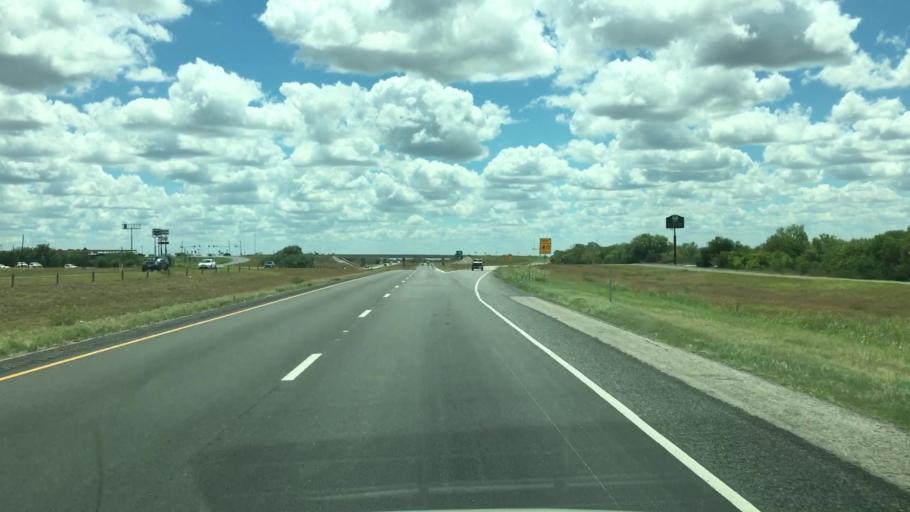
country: US
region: Texas
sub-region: Atascosa County
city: Pleasanton
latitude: 28.9995
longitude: -98.4313
